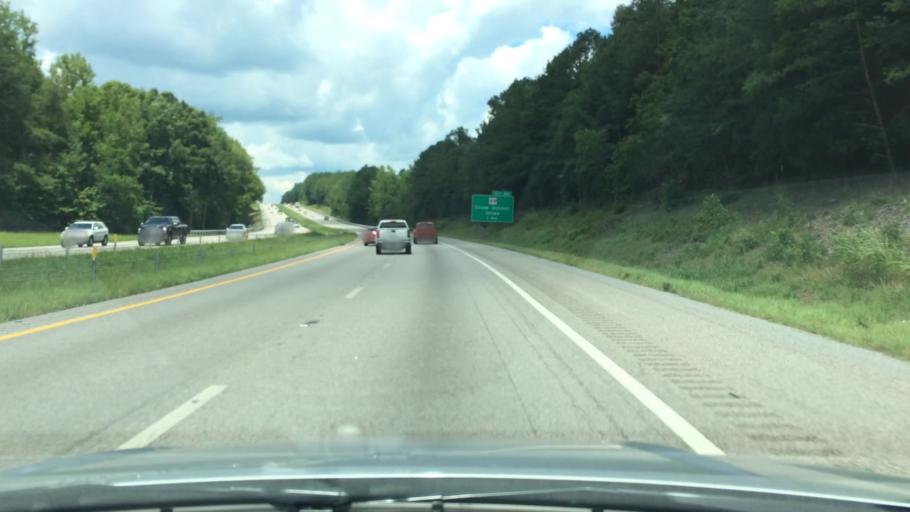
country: US
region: South Carolina
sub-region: Laurens County
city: Watts Mills
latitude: 34.6023
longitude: -81.8915
